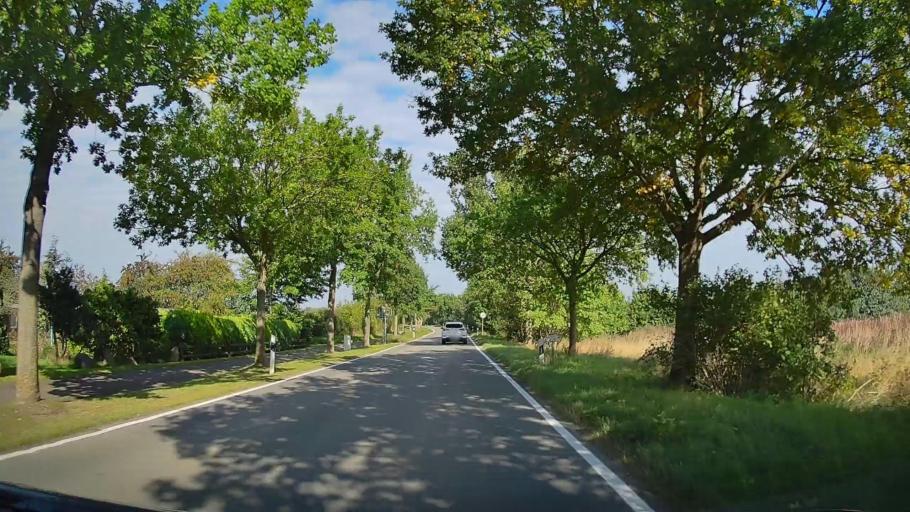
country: DE
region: Schleswig-Holstein
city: Oldenburg in Holstein
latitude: 54.3171
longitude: 10.8881
